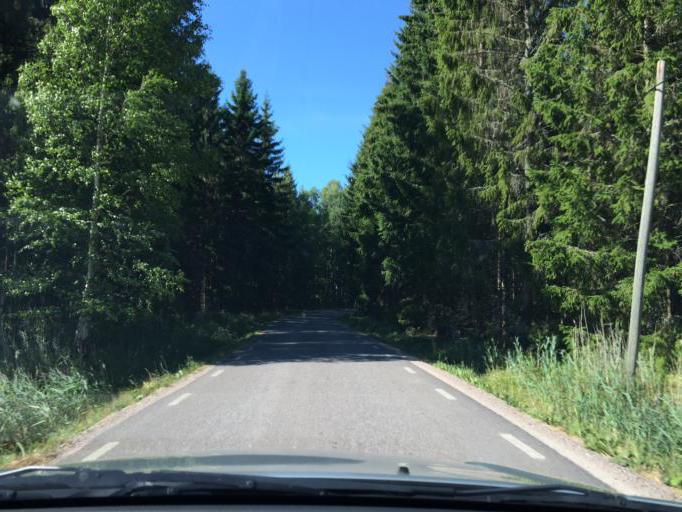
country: SE
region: Soedermanland
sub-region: Eskilstuna Kommun
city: Kvicksund
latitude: 59.4990
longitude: 16.3659
